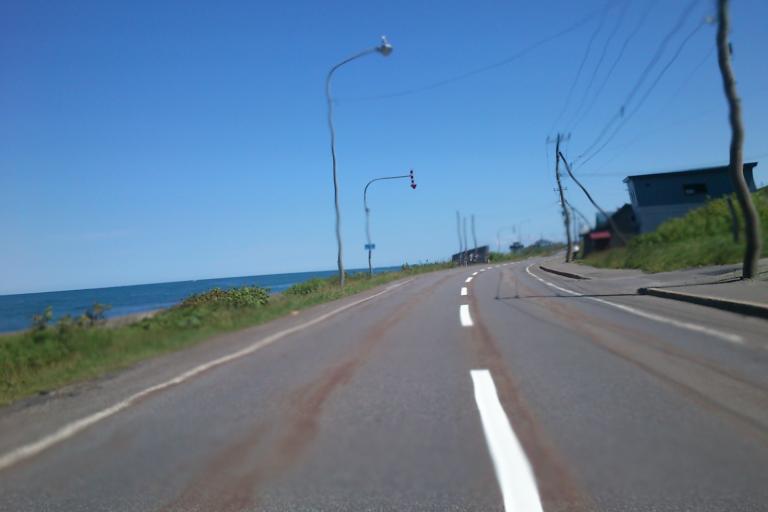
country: JP
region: Hokkaido
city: Rumoi
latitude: 43.8408
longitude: 141.4989
